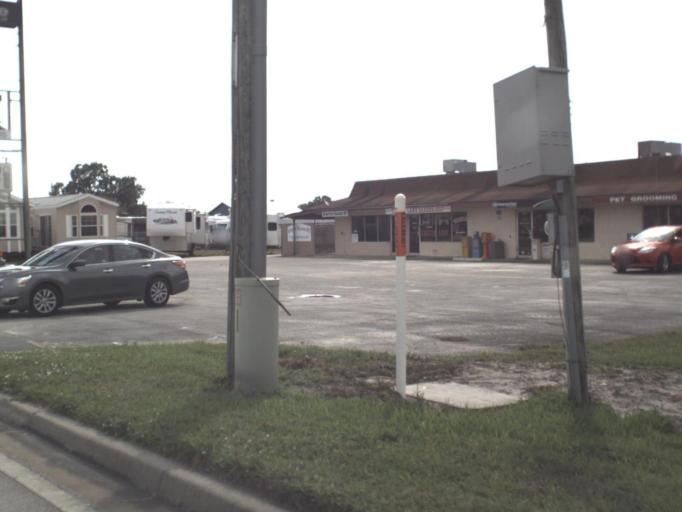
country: US
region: Florida
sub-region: Okeechobee County
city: Okeechobee
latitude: 27.2056
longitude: -80.8299
